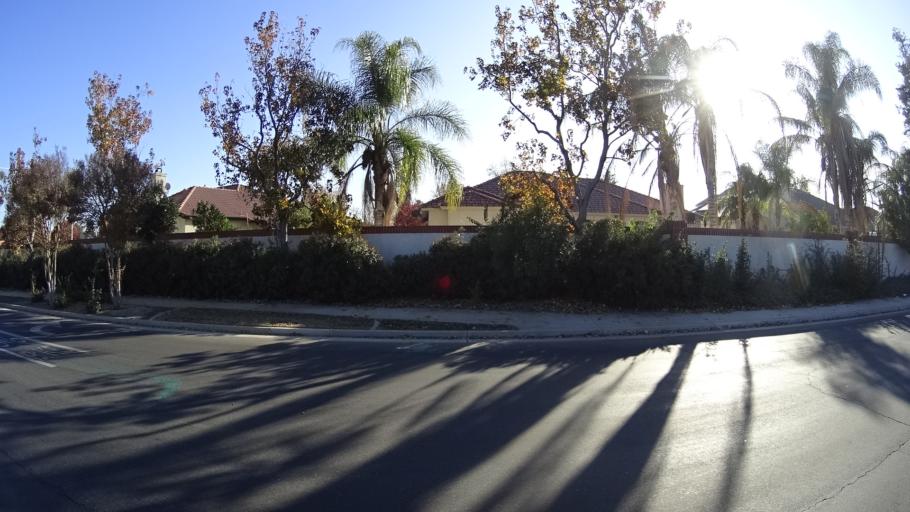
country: US
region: California
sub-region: Kern County
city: Rosedale
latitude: 35.3398
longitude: -119.1290
